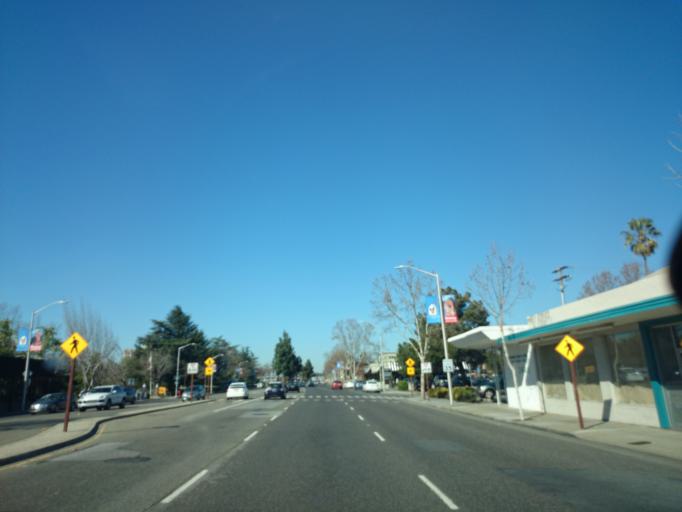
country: US
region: California
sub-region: Santa Clara County
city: Palo Alto
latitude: 37.4194
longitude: -122.1349
